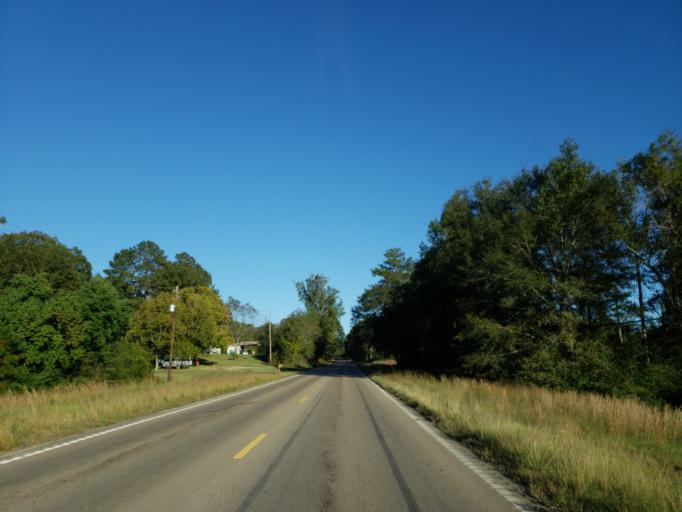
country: US
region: Mississippi
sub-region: Perry County
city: Richton
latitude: 31.3564
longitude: -88.9182
